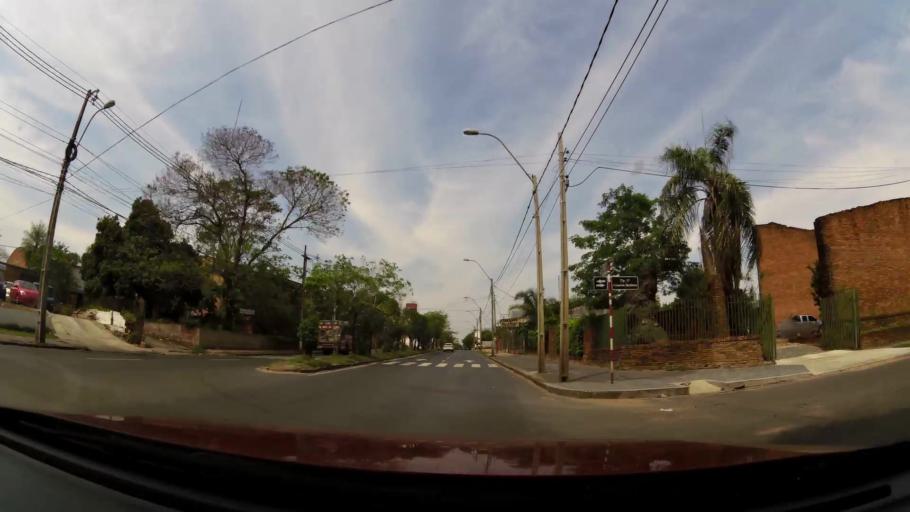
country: PY
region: Asuncion
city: Asuncion
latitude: -25.2639
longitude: -57.5820
